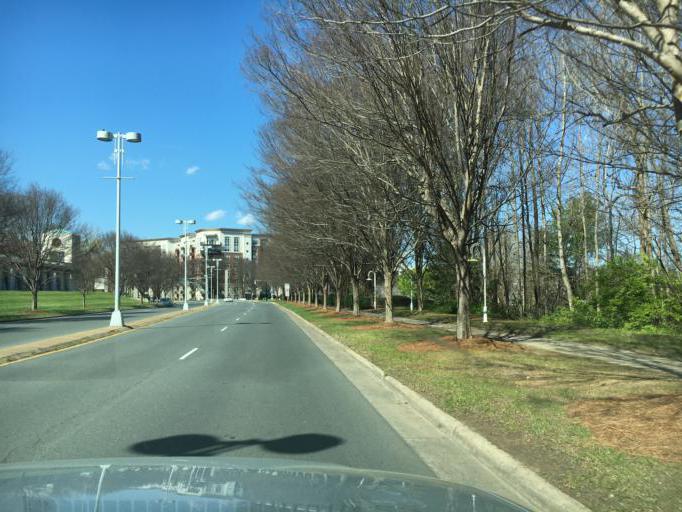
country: US
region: North Carolina
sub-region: Mecklenburg County
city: Charlotte
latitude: 35.1542
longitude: -80.8360
